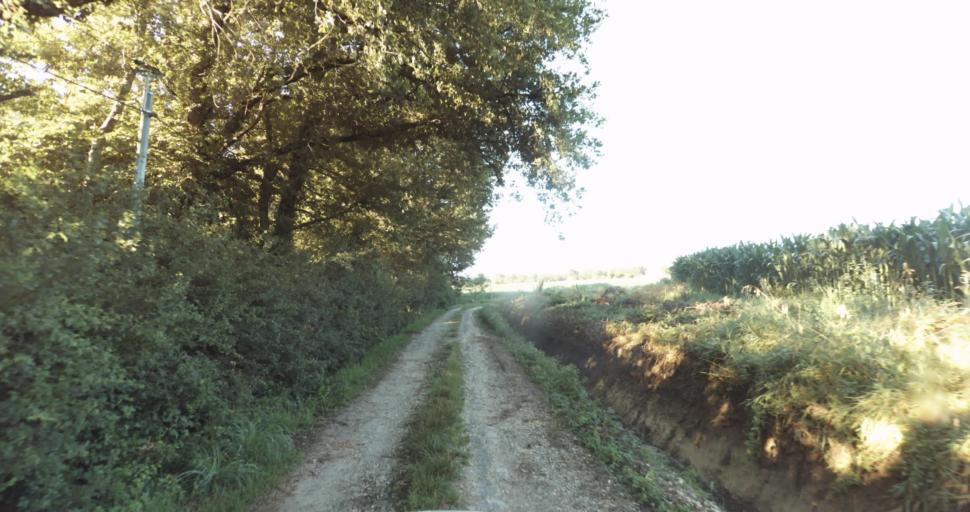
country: FR
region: Aquitaine
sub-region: Departement de la Gironde
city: Bazas
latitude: 44.4242
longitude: -0.2235
